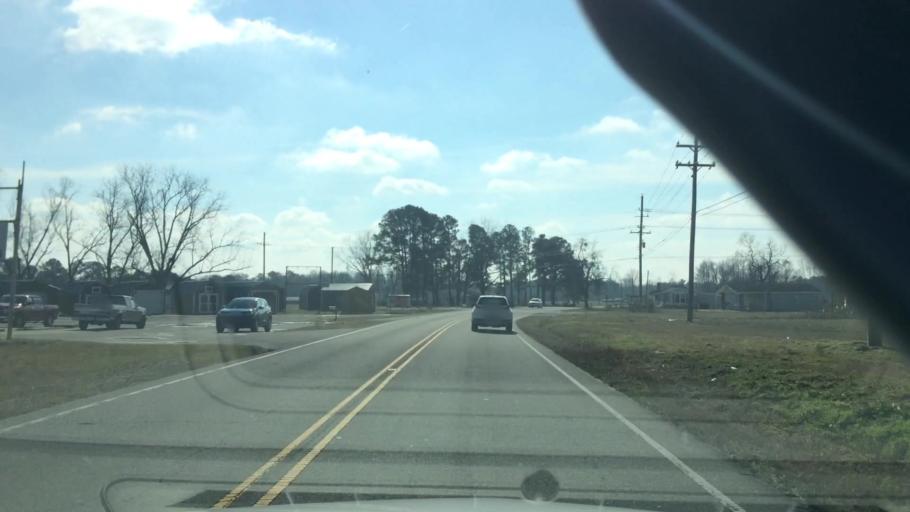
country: US
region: North Carolina
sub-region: Duplin County
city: Beulaville
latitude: 34.8881
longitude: -77.7843
